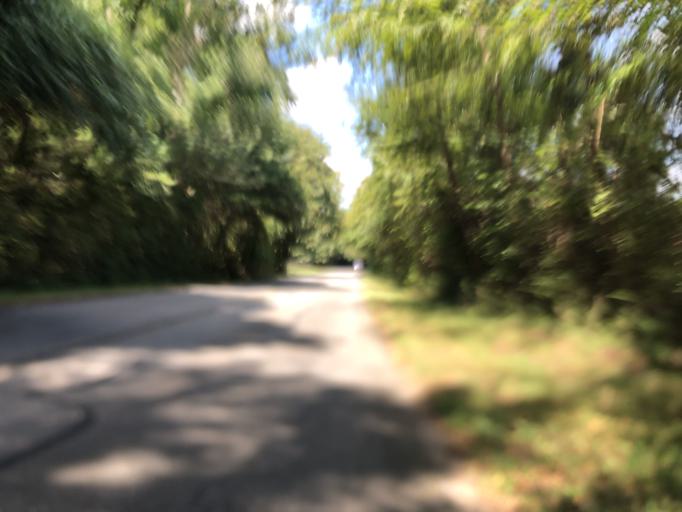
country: US
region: Georgia
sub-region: Fulton County
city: Palmetto
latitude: 33.5126
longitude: -84.6929
